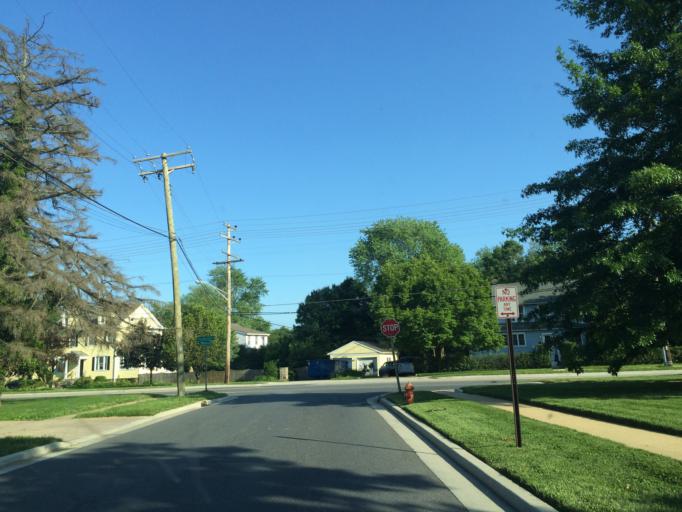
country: US
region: Maryland
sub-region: Baltimore County
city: Catonsville
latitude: 39.2698
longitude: -76.7440
